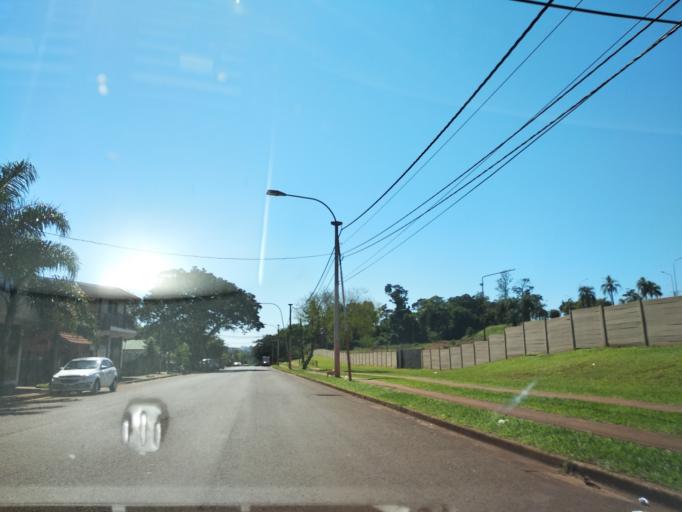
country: AR
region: Misiones
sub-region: Departamento de Iguazu
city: Puerto Iguazu
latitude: -25.6007
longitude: -54.5671
